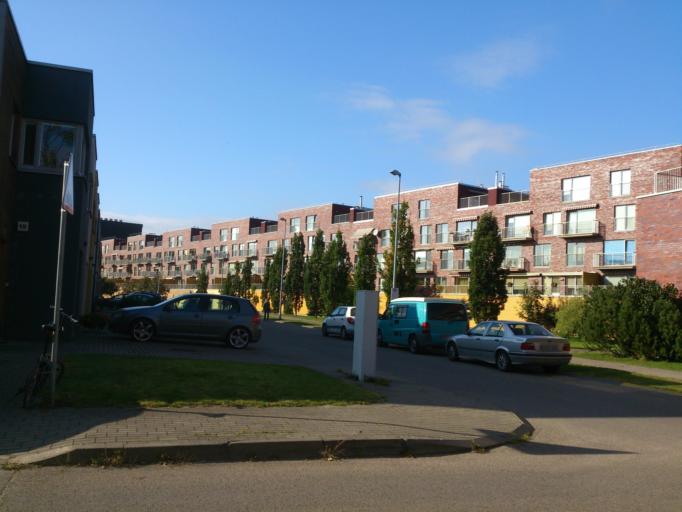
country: LT
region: Kauno apskritis
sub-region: Kaunas
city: Aleksotas
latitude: 54.8742
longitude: 23.9094
